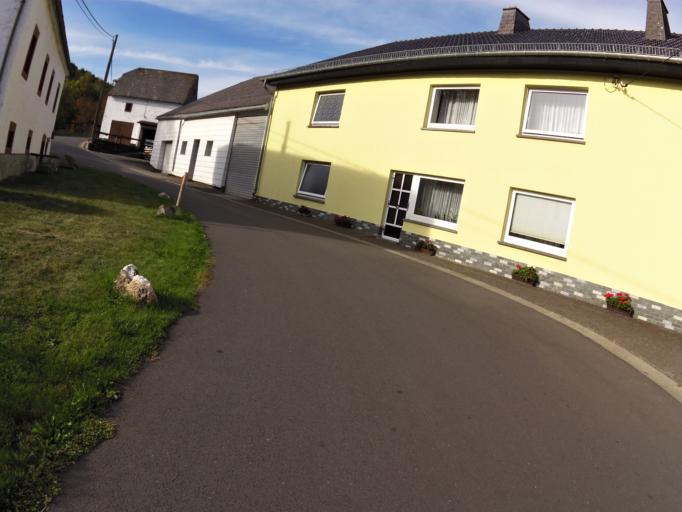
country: BE
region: Wallonia
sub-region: Province de Liege
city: Saint-Vith
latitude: 50.2552
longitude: 6.1469
